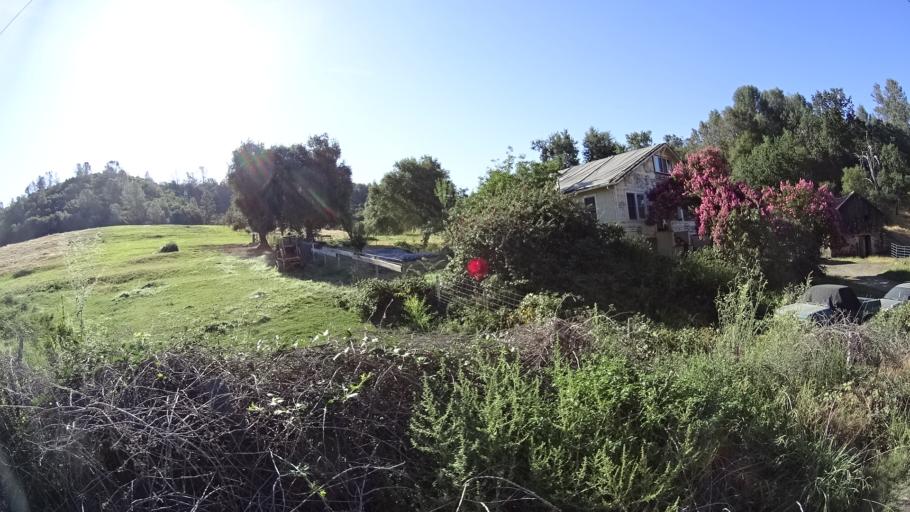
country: US
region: California
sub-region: Calaveras County
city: Angels Camp
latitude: 38.0575
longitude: -120.5055
